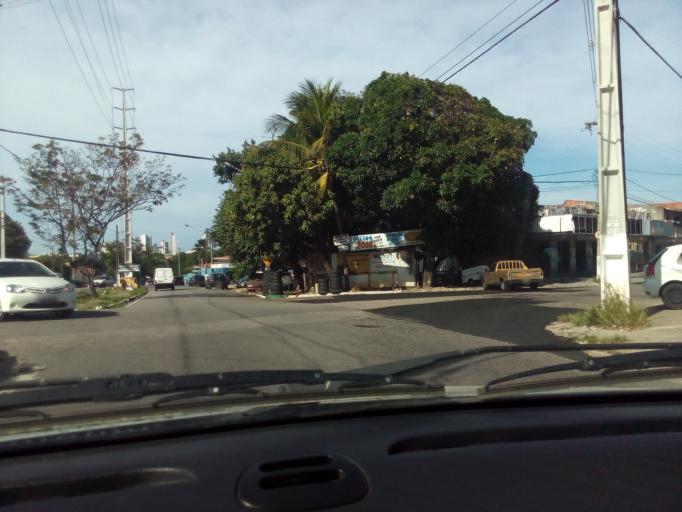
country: BR
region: Rio Grande do Norte
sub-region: Parnamirim
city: Parnamirim
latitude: -5.8712
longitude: -35.2083
